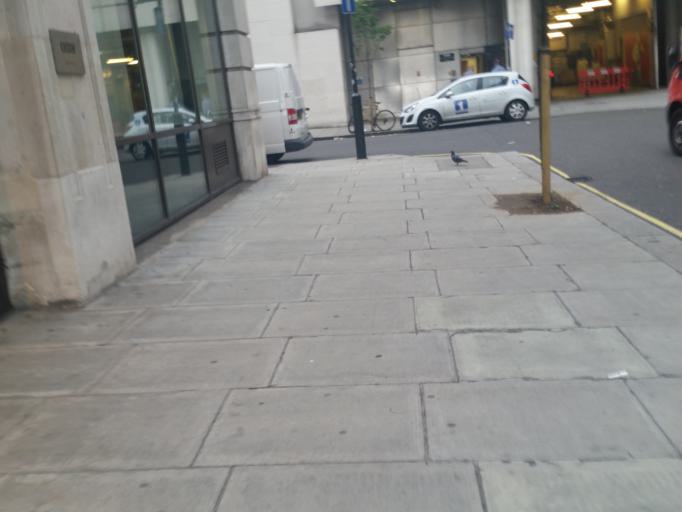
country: GB
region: England
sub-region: Greater London
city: London
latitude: 51.5188
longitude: -0.1430
